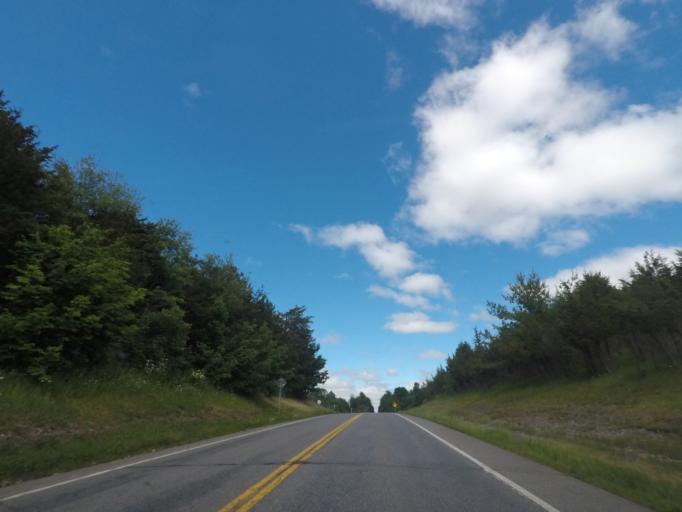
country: US
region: New York
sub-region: Columbia County
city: Philmont
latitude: 42.2083
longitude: -73.6611
